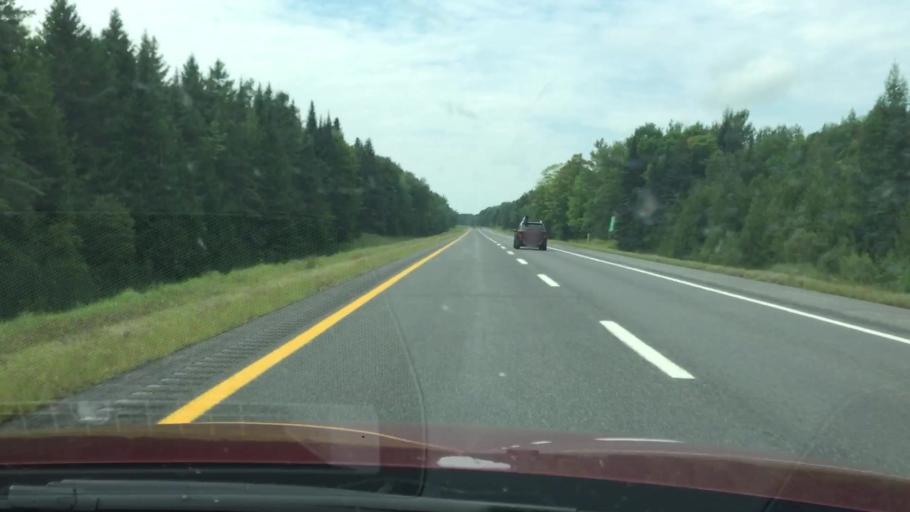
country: US
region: Maine
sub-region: Aroostook County
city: Houlton
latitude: 46.1387
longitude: -67.9186
